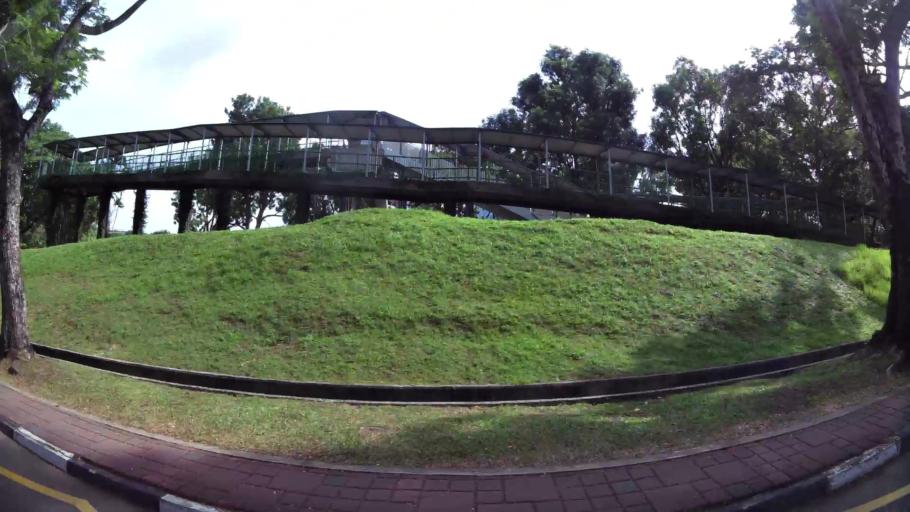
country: SG
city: Singapore
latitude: 1.2958
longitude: 103.7840
